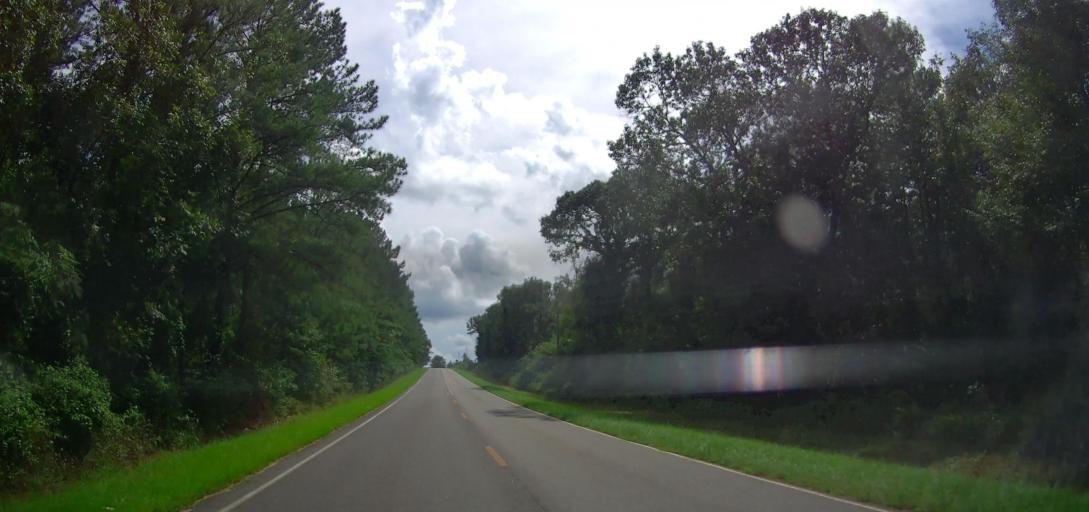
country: US
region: Georgia
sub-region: Taylor County
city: Butler
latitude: 32.4834
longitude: -84.2057
